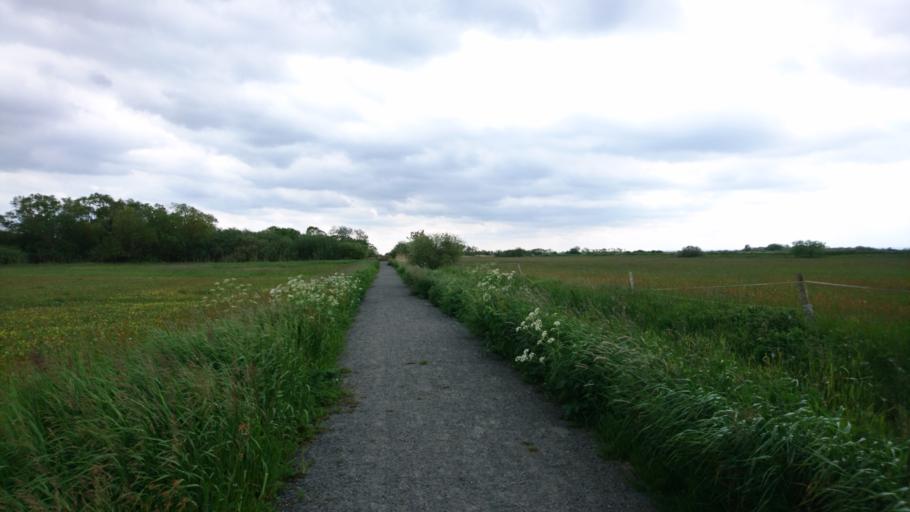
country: SE
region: Skane
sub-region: Kristianstads Kommun
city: Fjalkinge
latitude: 56.0047
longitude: 14.2413
